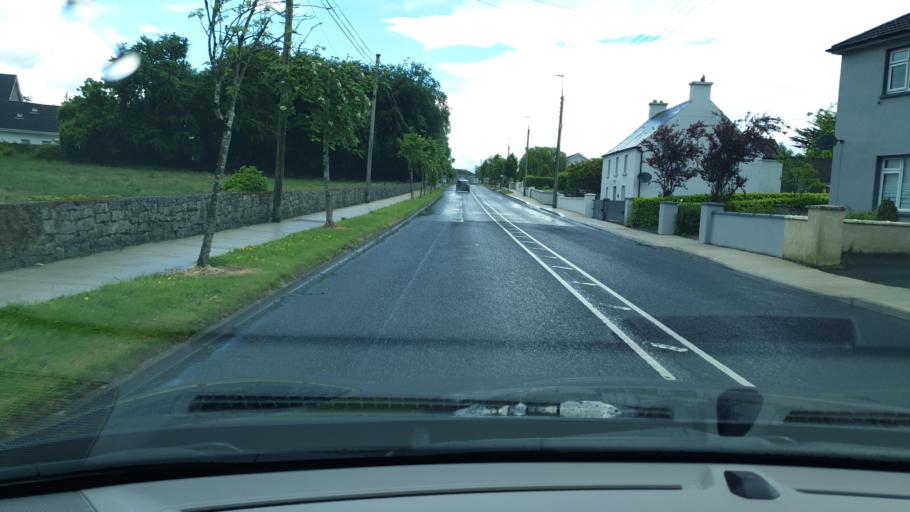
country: IE
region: Connaught
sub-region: County Galway
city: Ballinasloe
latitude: 53.3257
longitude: -8.1969
